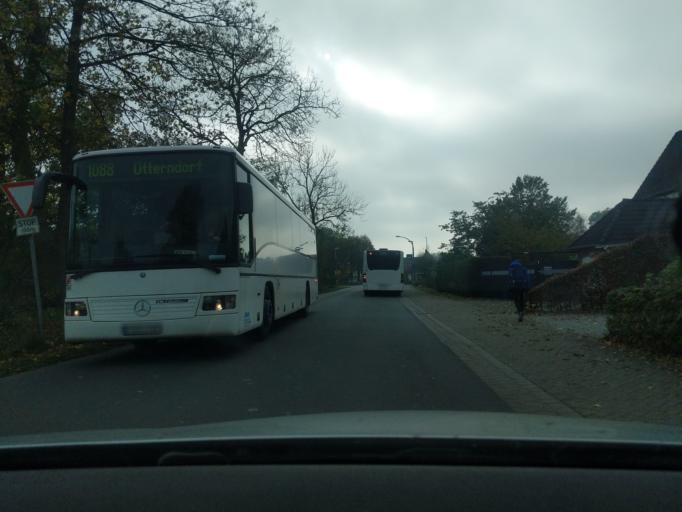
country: DE
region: Lower Saxony
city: Wanna
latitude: 53.8008
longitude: 8.7545
